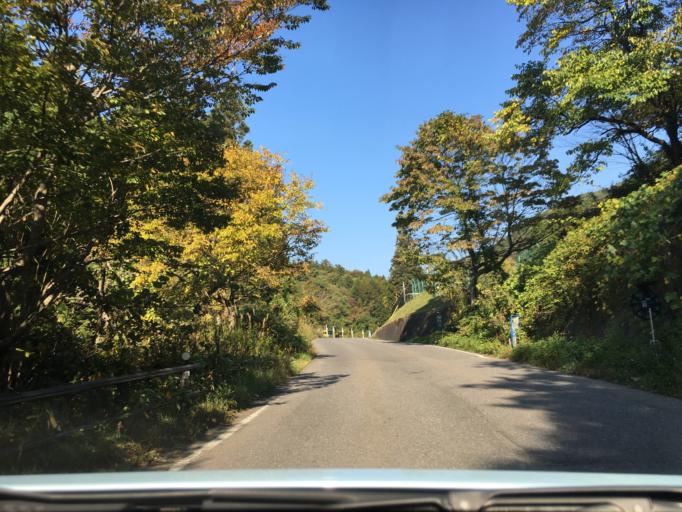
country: JP
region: Fukushima
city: Sukagawa
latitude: 37.3062
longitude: 140.1456
